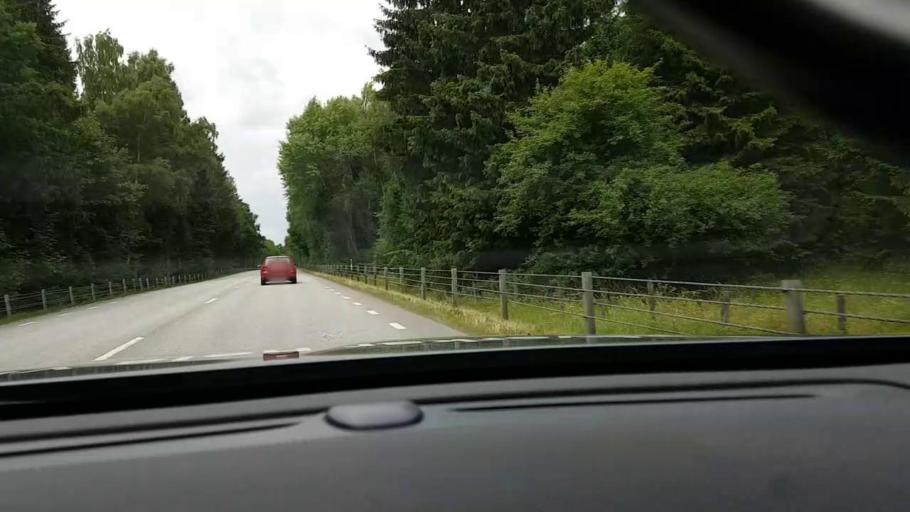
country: SE
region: Skane
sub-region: Hoors Kommun
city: Satofta
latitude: 55.9119
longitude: 13.6002
